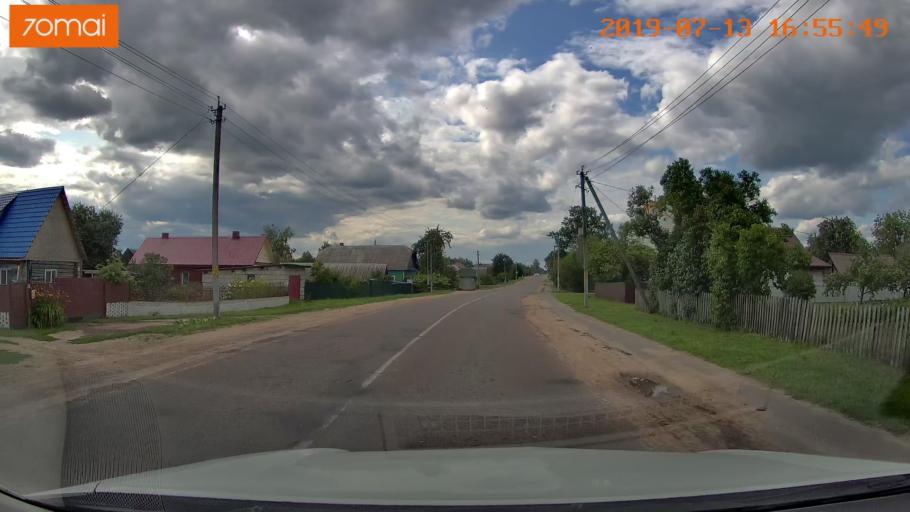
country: BY
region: Mogilev
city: Kirawsk
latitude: 53.2696
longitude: 29.4637
